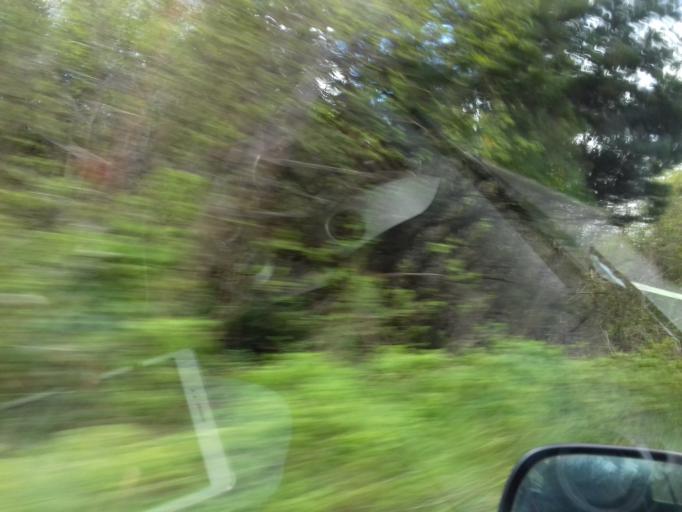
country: IE
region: Leinster
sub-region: Loch Garman
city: Loch Garman
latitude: 52.3099
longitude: -6.5442
